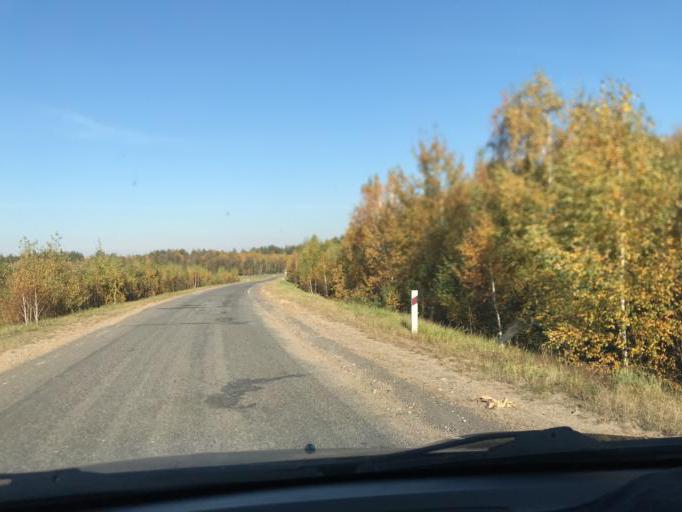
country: BY
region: Mogilev
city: Babruysk
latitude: 53.1032
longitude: 29.0574
